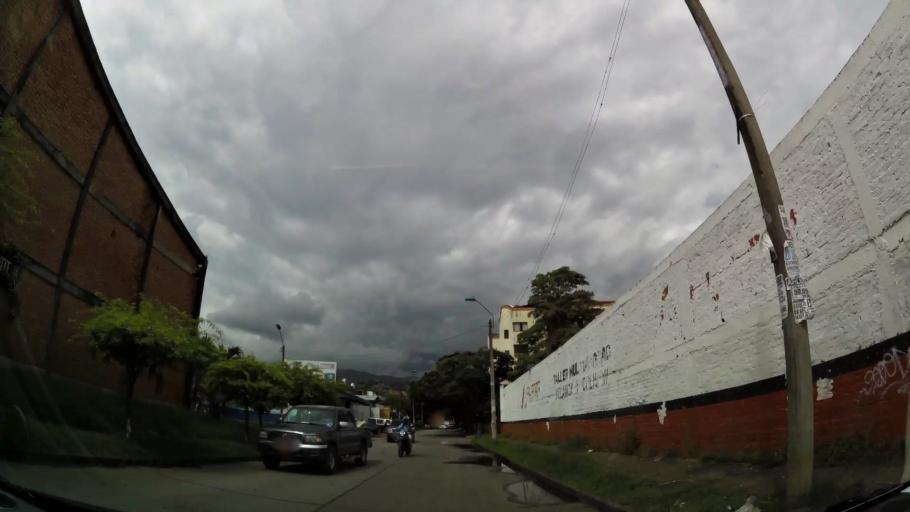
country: CO
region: Valle del Cauca
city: Cali
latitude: 3.3961
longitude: -76.5474
